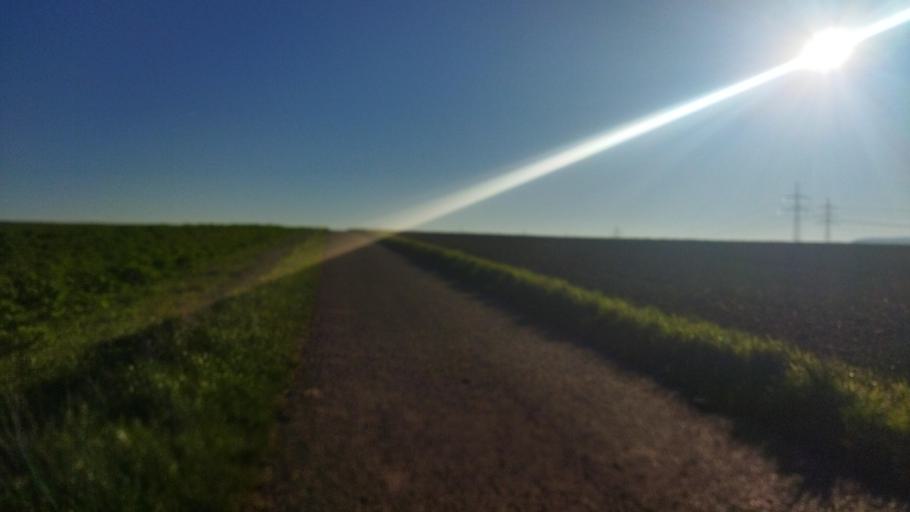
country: DE
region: Baden-Wuerttemberg
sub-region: Regierungsbezirk Stuttgart
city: Lauffen am Neckar
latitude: 49.0766
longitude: 9.1258
